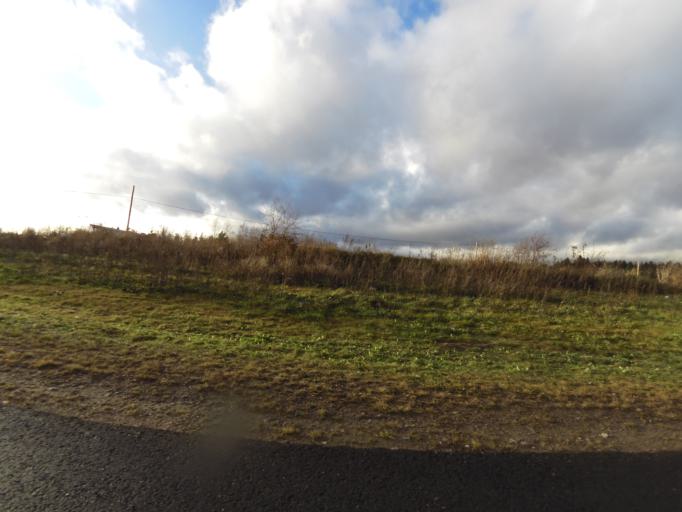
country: FI
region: Uusimaa
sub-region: Helsinki
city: Kilo
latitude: 60.2020
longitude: 24.7872
